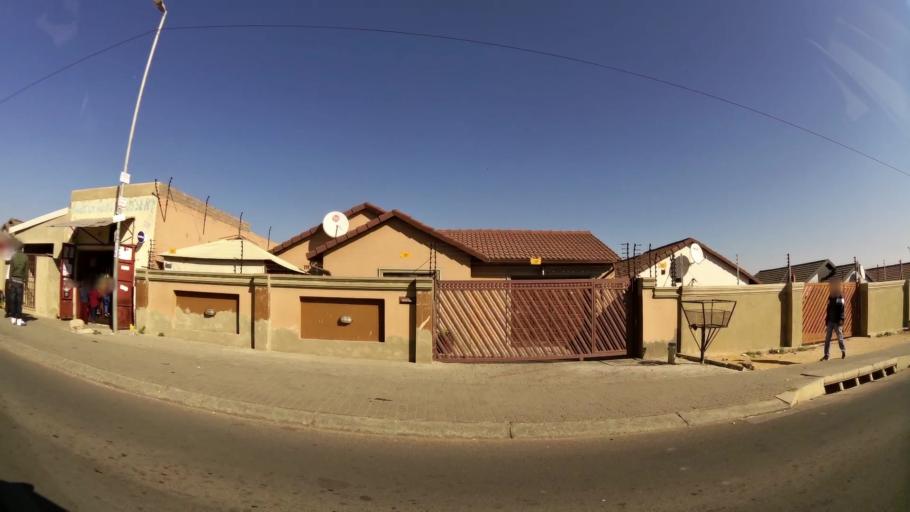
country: ZA
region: Gauteng
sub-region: City of Johannesburg Metropolitan Municipality
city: Modderfontein
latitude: -26.0441
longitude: 28.1963
